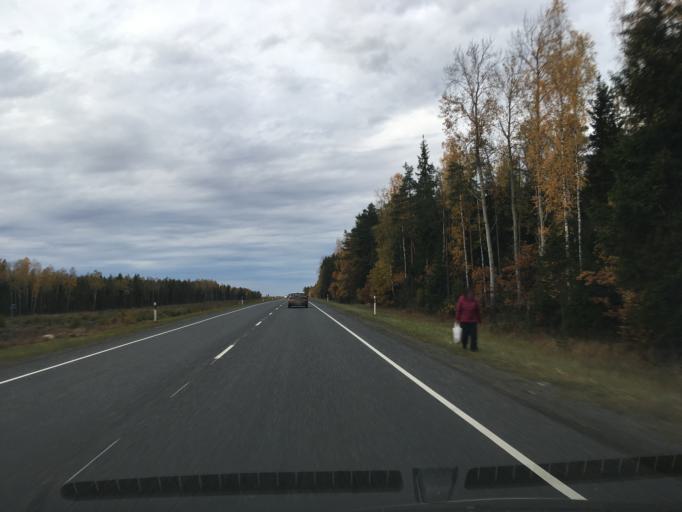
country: EE
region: Harju
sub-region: Nissi vald
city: Turba
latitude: 58.9560
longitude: 24.0778
